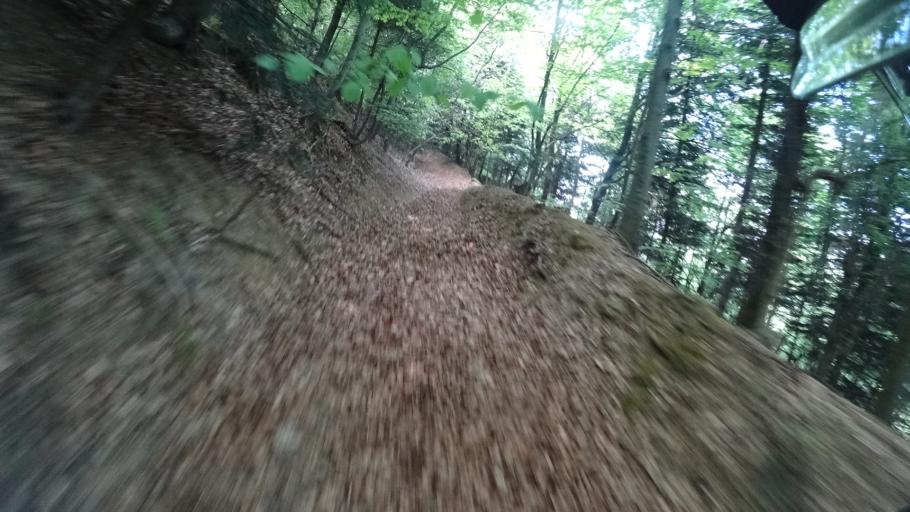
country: HR
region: Grad Zagreb
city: Kasina
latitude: 45.9241
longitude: 15.9512
